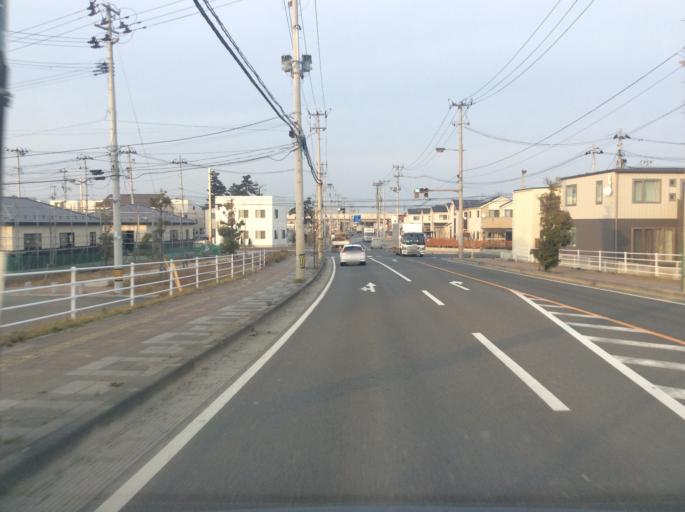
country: JP
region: Miyagi
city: Iwanuma
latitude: 38.1553
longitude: 140.9218
